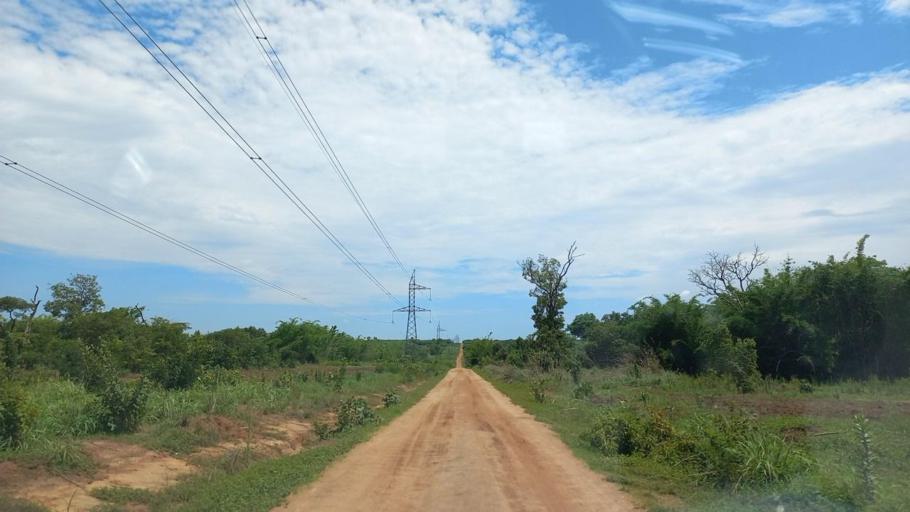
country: ZM
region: Copperbelt
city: Kitwe
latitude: -12.8168
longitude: 28.3559
